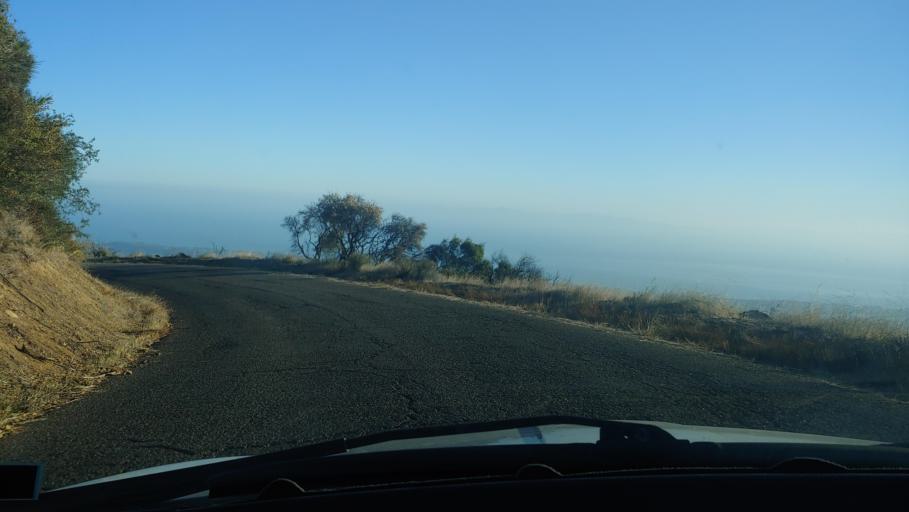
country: US
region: California
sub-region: Santa Barbara County
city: Mission Canyon
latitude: 34.5071
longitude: -119.7686
